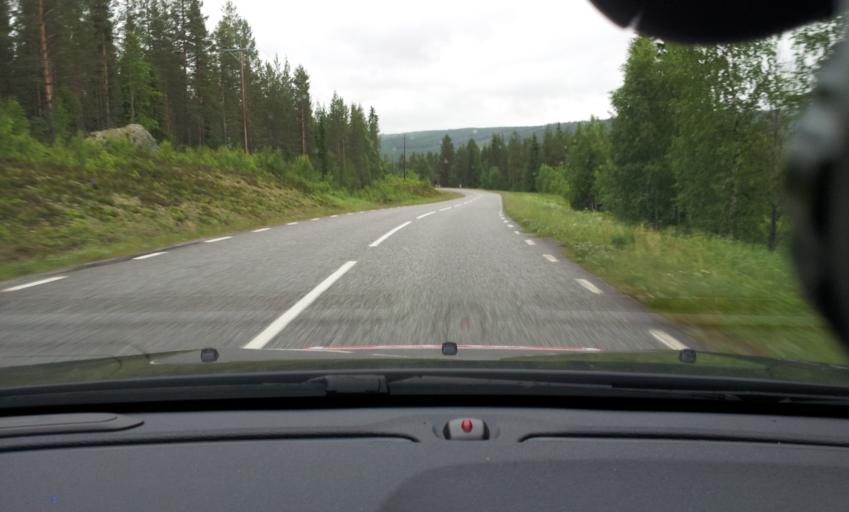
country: SE
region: Jaemtland
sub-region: Stroemsunds Kommun
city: Stroemsund
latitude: 63.2959
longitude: 15.7696
